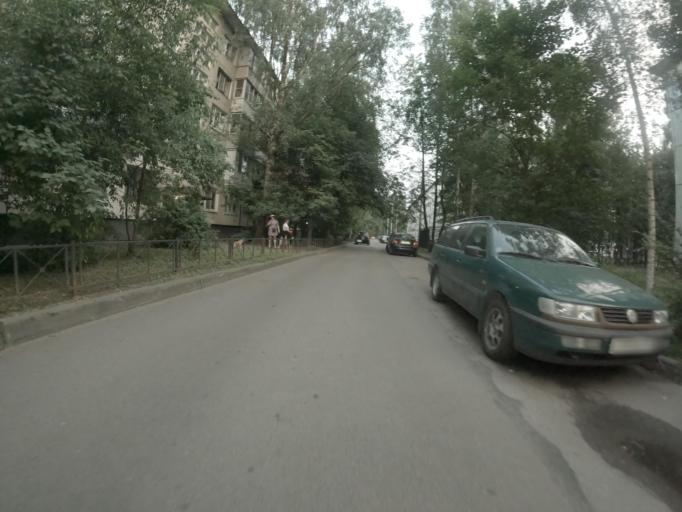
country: RU
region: St.-Petersburg
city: Krasnogvargeisky
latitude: 59.9578
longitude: 30.4441
